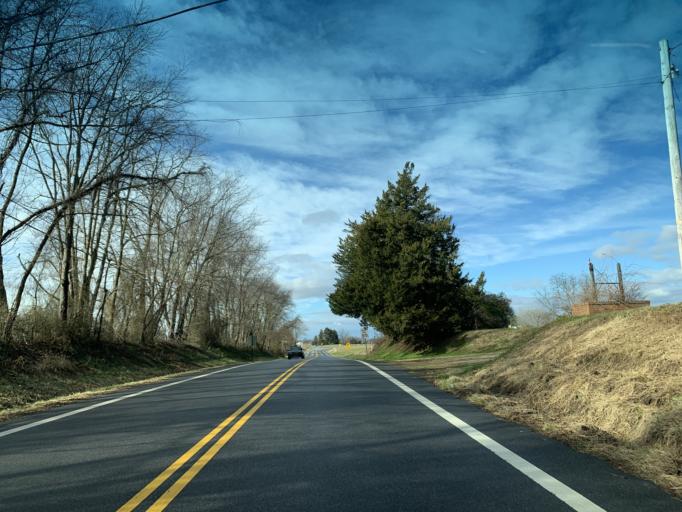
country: US
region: Maryland
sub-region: Kent County
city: Chestertown
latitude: 39.3294
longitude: -76.0560
